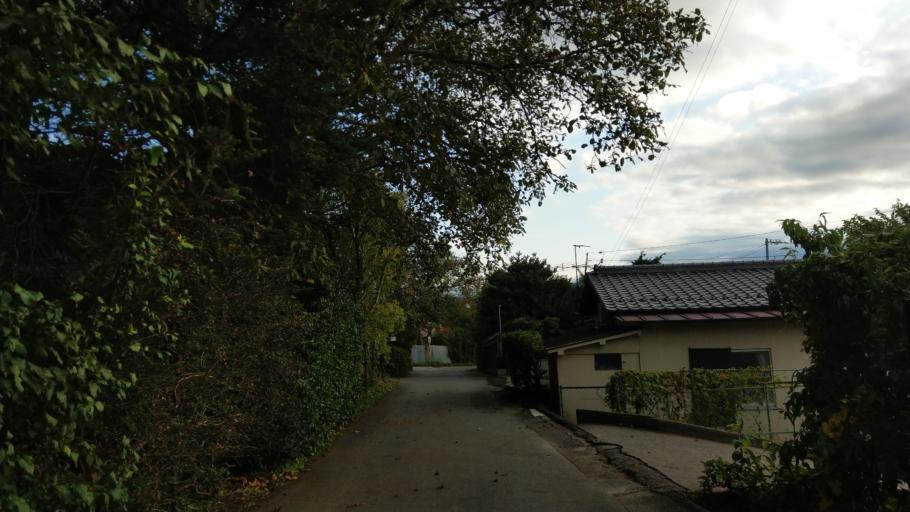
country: JP
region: Nagano
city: Komoro
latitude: 36.3360
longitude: 138.4195
